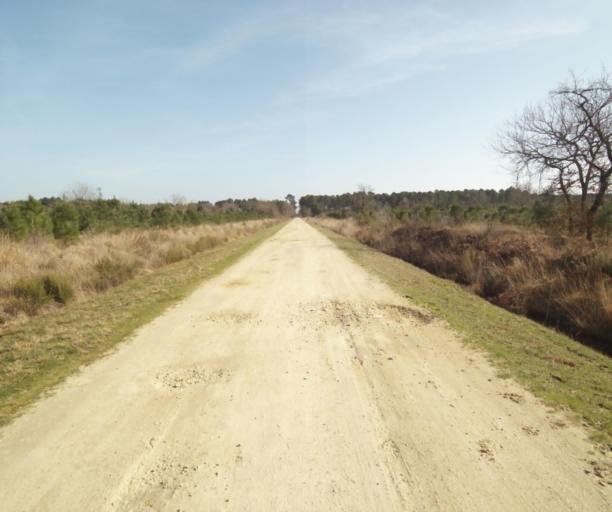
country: FR
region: Aquitaine
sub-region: Departement des Landes
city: Roquefort
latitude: 44.2230
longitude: -0.2304
